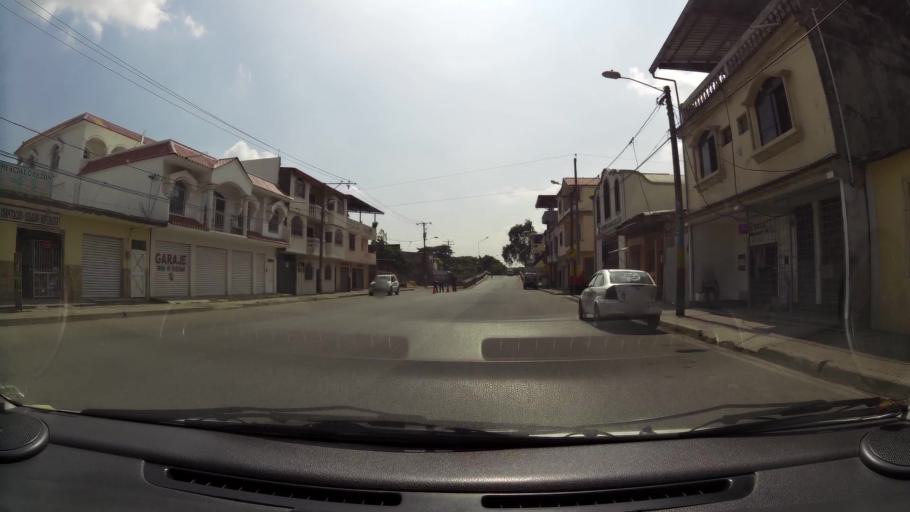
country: EC
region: Guayas
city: Eloy Alfaro
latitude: -2.1535
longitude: -79.8349
